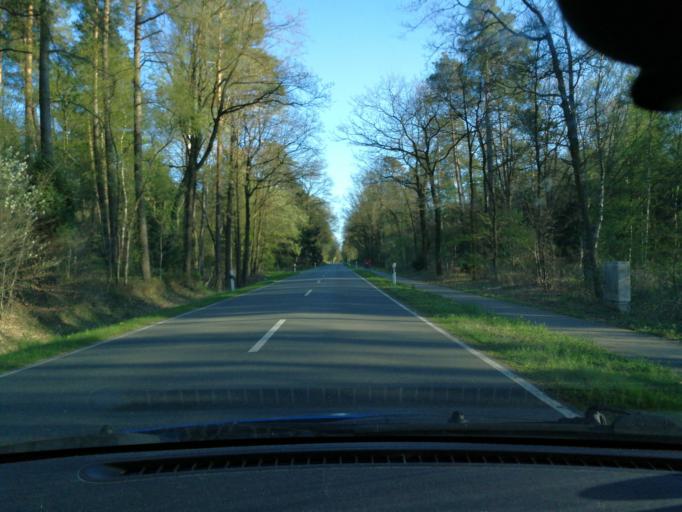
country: DE
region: Lower Saxony
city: Bispingen
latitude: 53.0740
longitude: 9.9940
